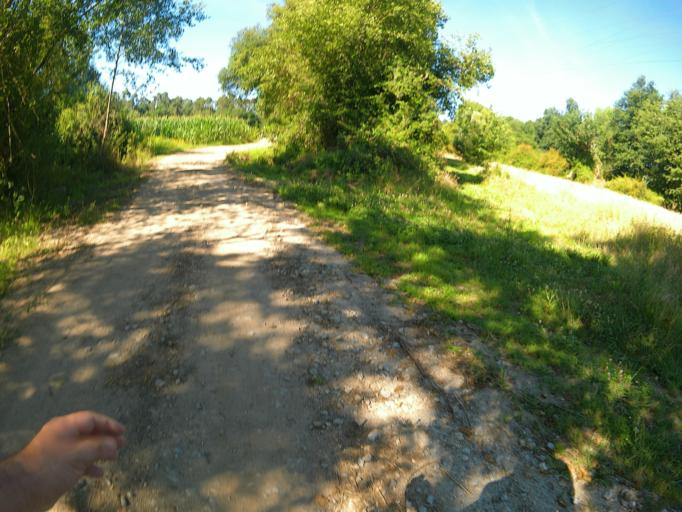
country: PT
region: Viana do Castelo
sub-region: Ponte de Lima
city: Ponte de Lima
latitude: 41.7288
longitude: -8.6658
